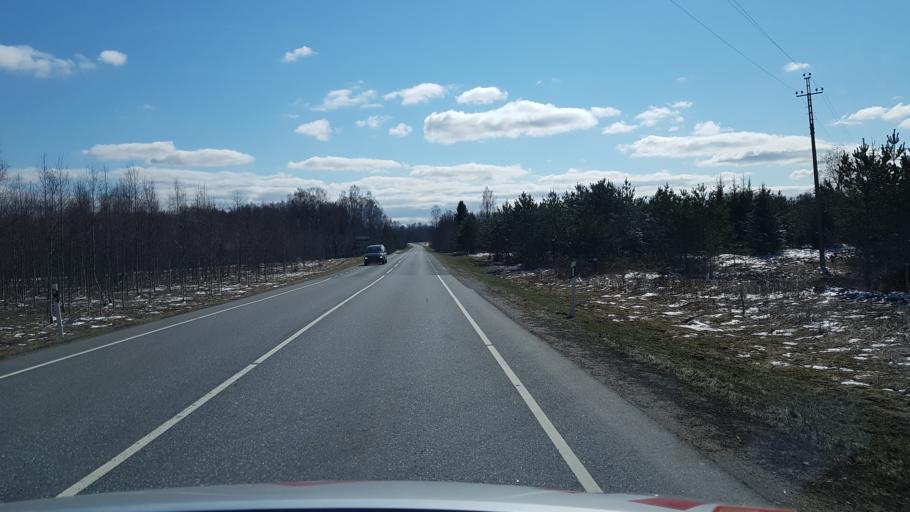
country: EE
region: Laeaene-Virumaa
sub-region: Tapa vald
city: Tapa
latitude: 59.4514
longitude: 25.9455
